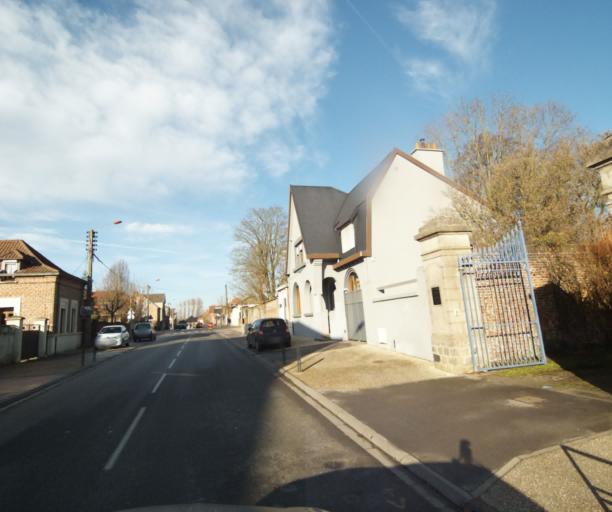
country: FR
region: Nord-Pas-de-Calais
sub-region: Departement du Nord
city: Preseau
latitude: 50.3123
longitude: 3.5762
